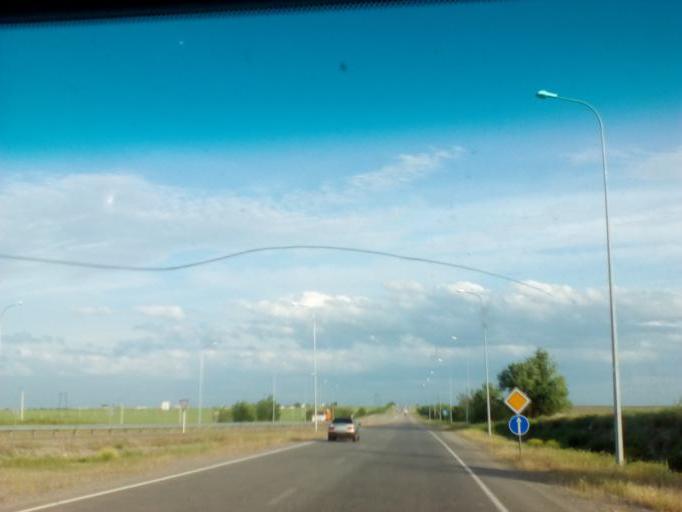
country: KZ
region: Ongtustik Qazaqstan
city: Temirlanovka
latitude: 42.5256
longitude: 69.3437
